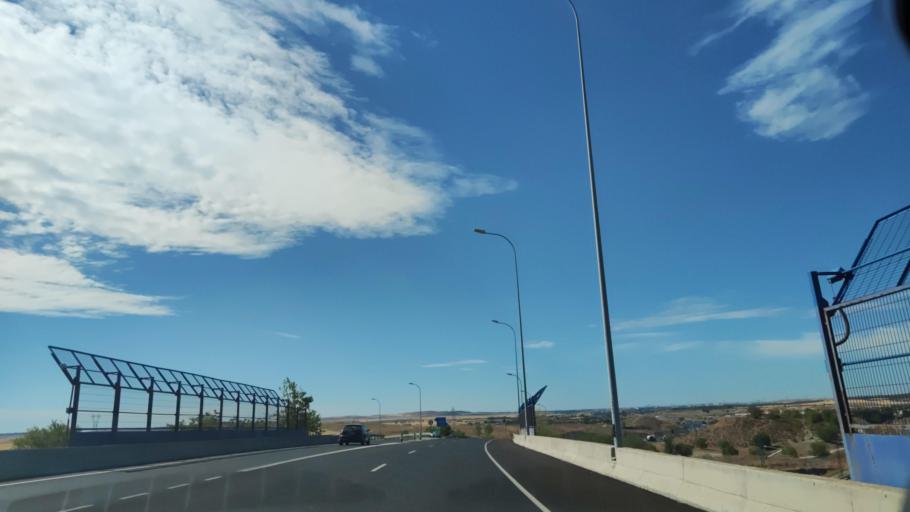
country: ES
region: Madrid
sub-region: Provincia de Madrid
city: Villa de Vallecas
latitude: 40.3355
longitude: -3.6302
